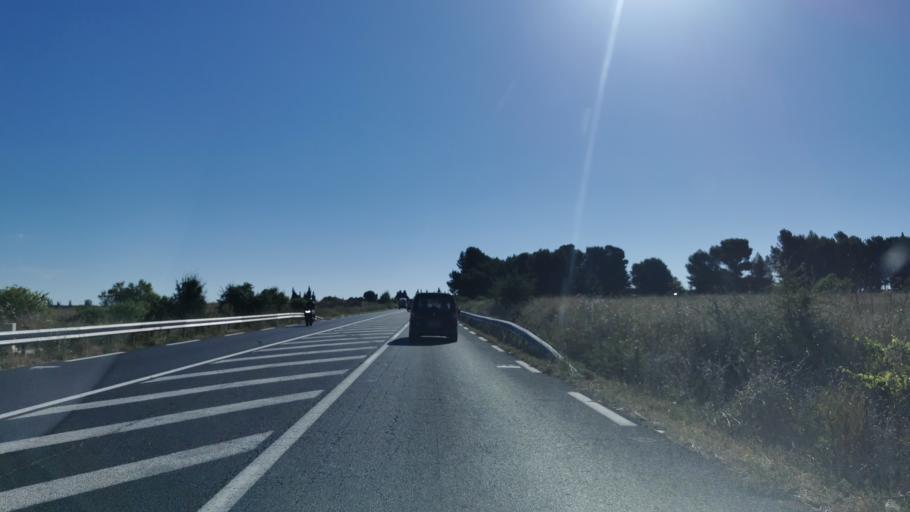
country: FR
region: Languedoc-Roussillon
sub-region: Departement de l'Herault
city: Nissan-lez-Enserune
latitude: 43.2959
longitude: 3.1437
